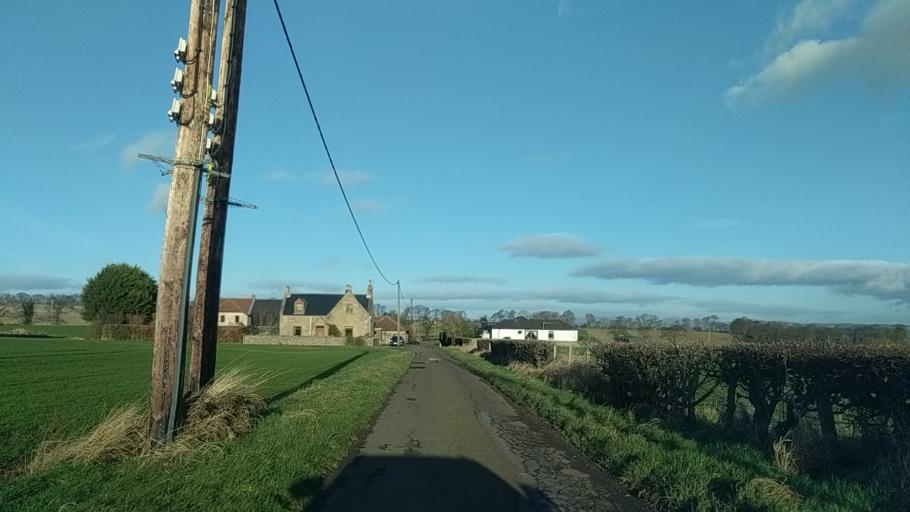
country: GB
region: Scotland
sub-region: West Lothian
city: Linlithgow
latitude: 55.9950
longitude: -3.5437
